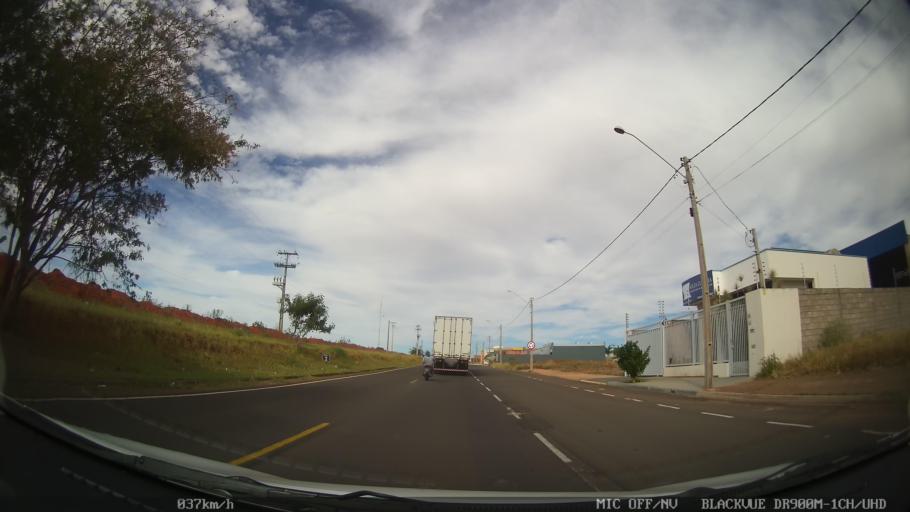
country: BR
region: Sao Paulo
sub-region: Catanduva
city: Catanduva
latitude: -21.1587
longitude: -48.9631
